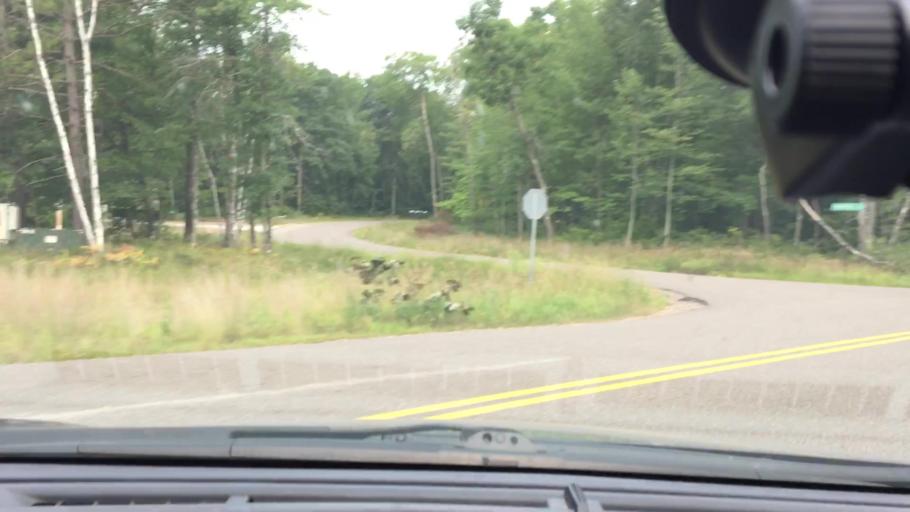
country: US
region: Minnesota
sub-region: Crow Wing County
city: Cross Lake
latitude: 46.6668
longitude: -94.0426
